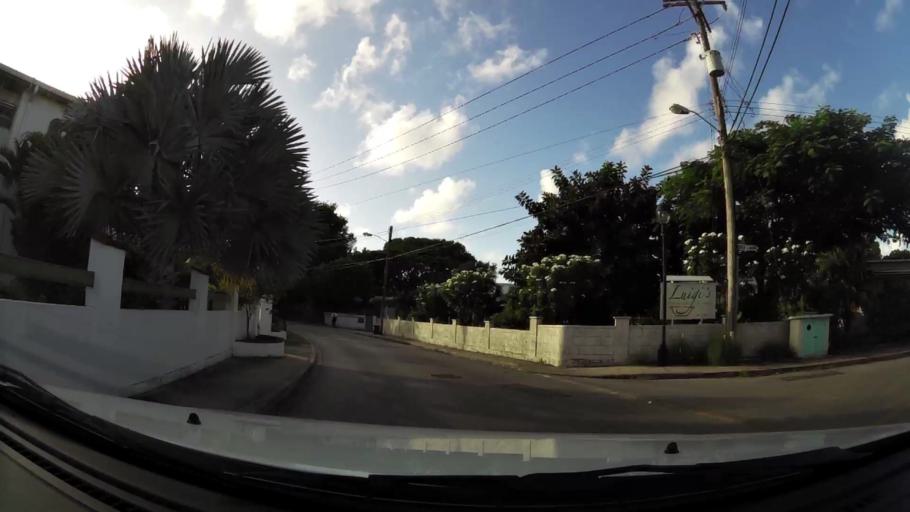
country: BB
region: Christ Church
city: Oistins
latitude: 13.0678
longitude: -59.5645
